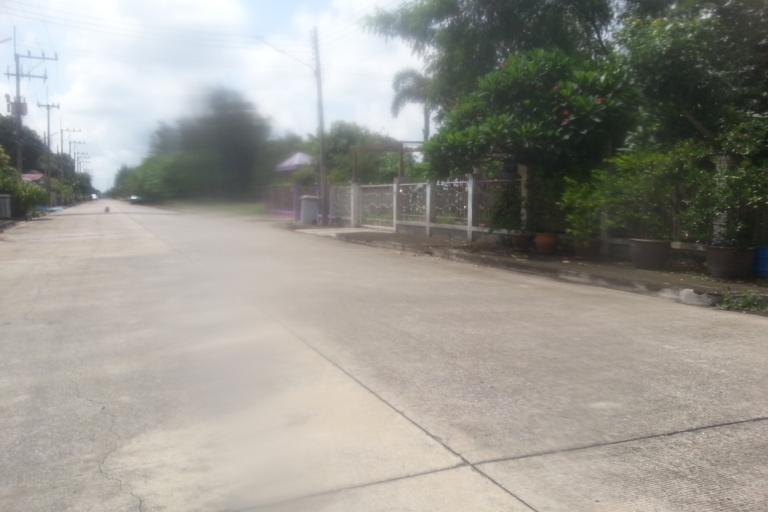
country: TH
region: Pathum Thani
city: Nong Suea
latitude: 14.0481
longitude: 100.8606
